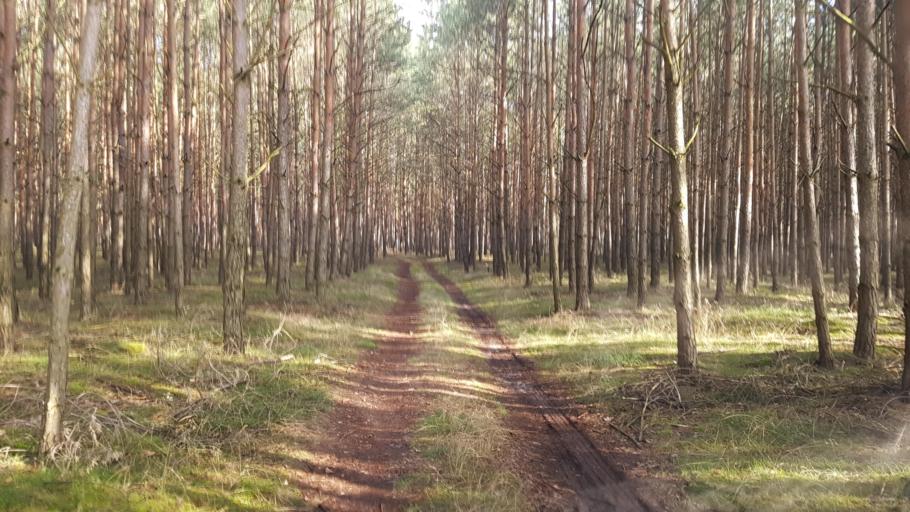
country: DE
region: Brandenburg
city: Schonewalde
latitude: 51.7062
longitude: 13.5890
